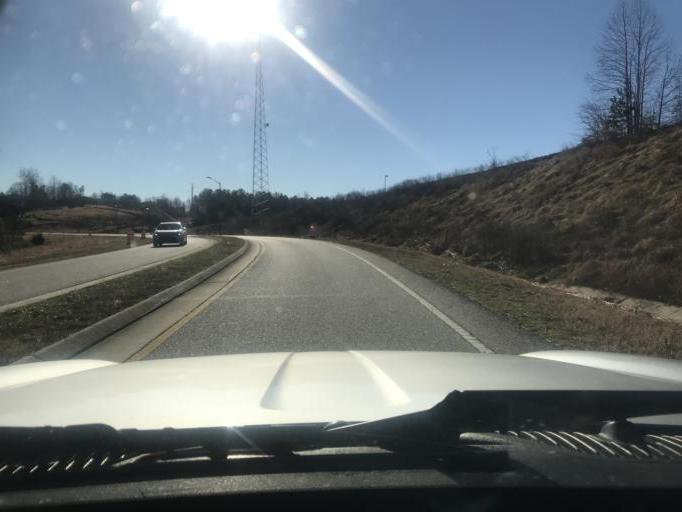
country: US
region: Georgia
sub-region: Barrow County
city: Winder
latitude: 34.0020
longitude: -83.7585
